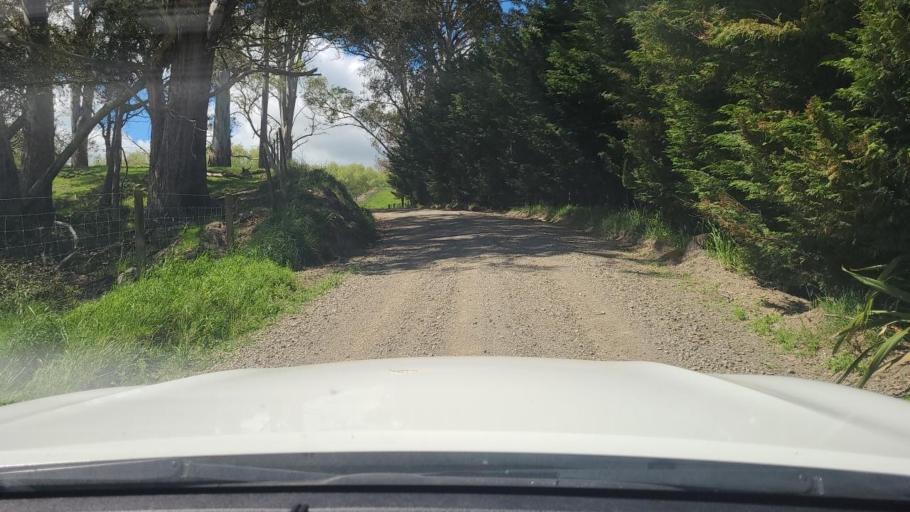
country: NZ
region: Hawke's Bay
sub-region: Napier City
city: Napier
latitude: -39.1506
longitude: 176.6552
